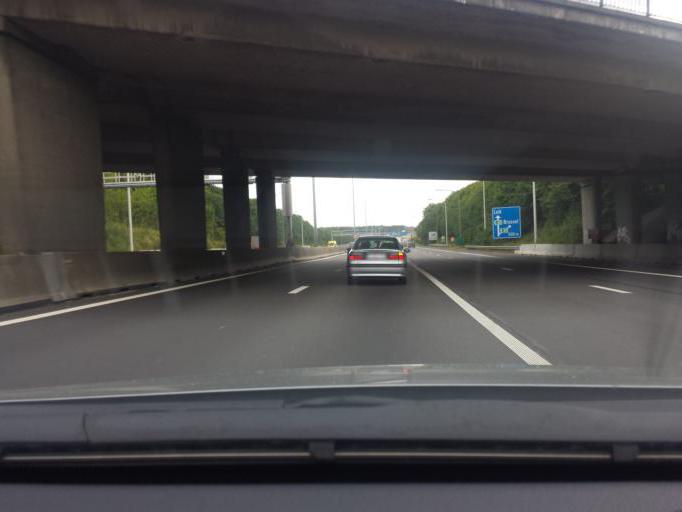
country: BE
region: Flanders
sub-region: Provincie Vlaams-Brabant
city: Bertem
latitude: 50.8655
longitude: 4.6504
